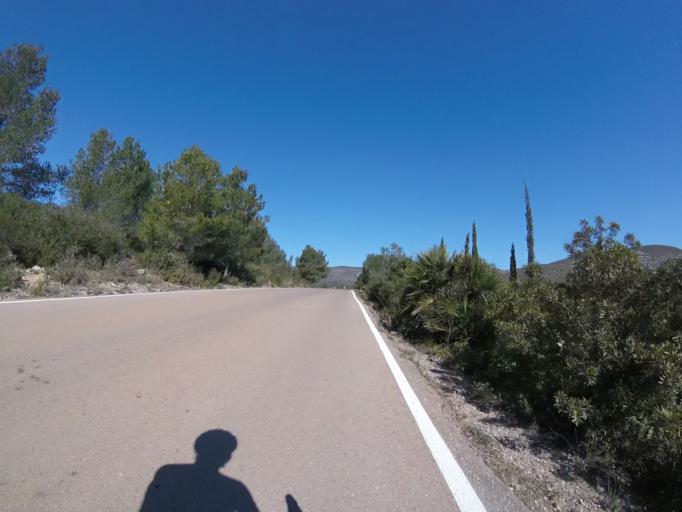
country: ES
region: Valencia
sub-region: Provincia de Castello
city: Santa Magdalena de Pulpis
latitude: 40.3678
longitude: 0.2753
